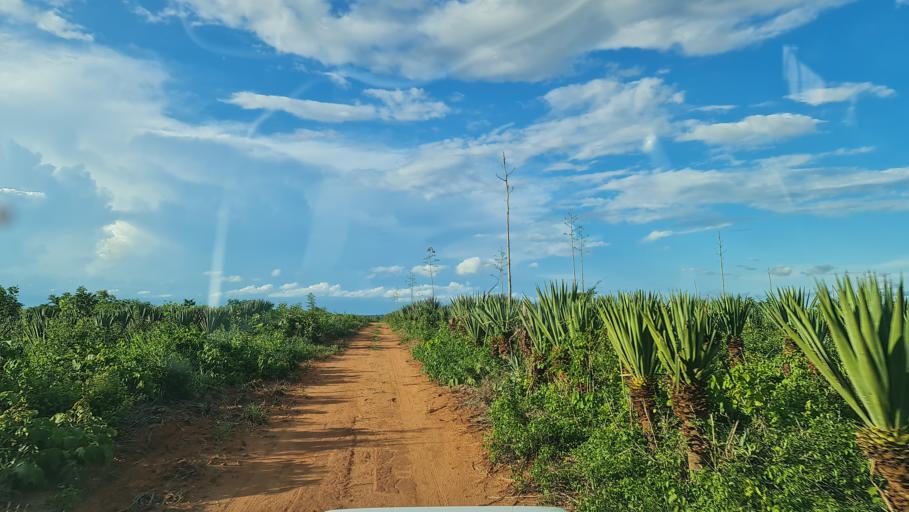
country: MZ
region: Nampula
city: Ilha de Mocambique
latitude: -14.9541
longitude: 40.1846
